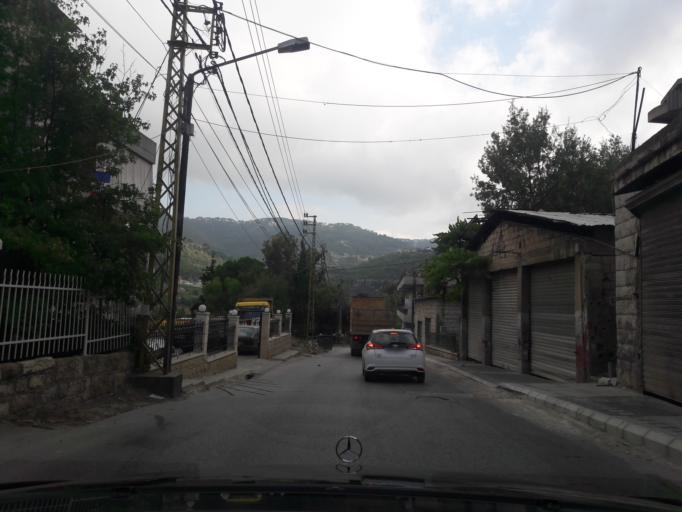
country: LB
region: Mont-Liban
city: Djounie
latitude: 33.9266
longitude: 35.7314
